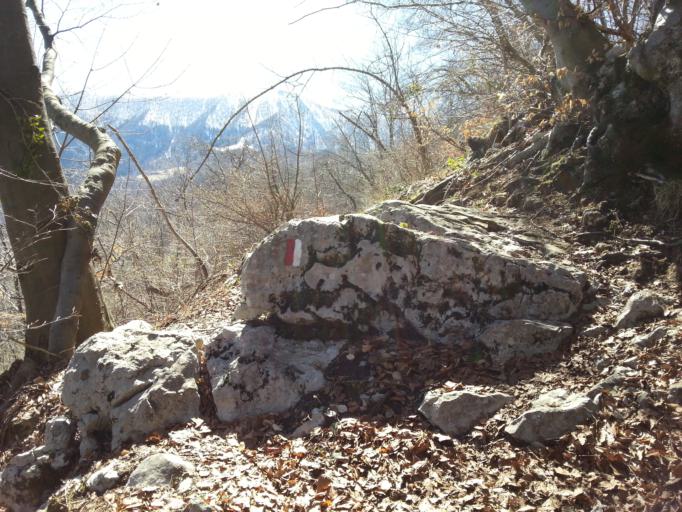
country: IT
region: Lombardy
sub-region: Provincia di Como
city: Magreglio
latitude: 45.9396
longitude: 9.2270
